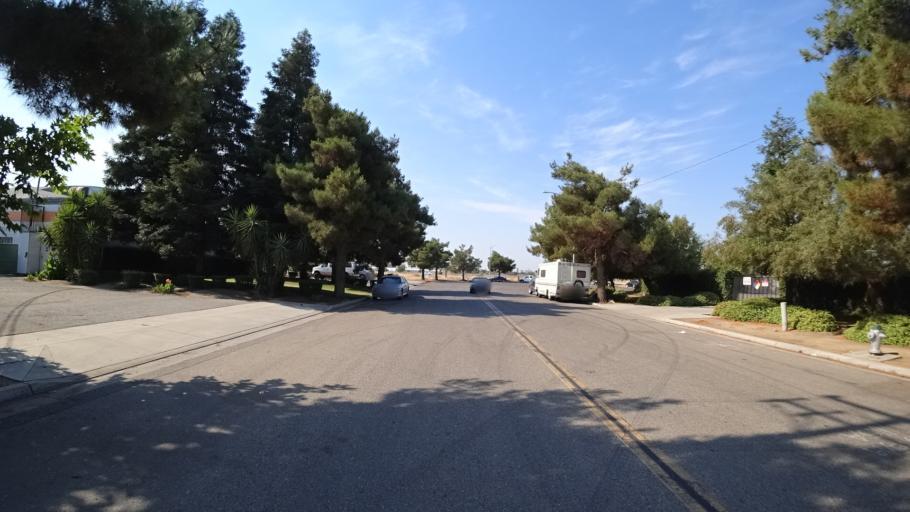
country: US
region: California
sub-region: Fresno County
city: West Park
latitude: 36.7394
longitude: -119.8265
